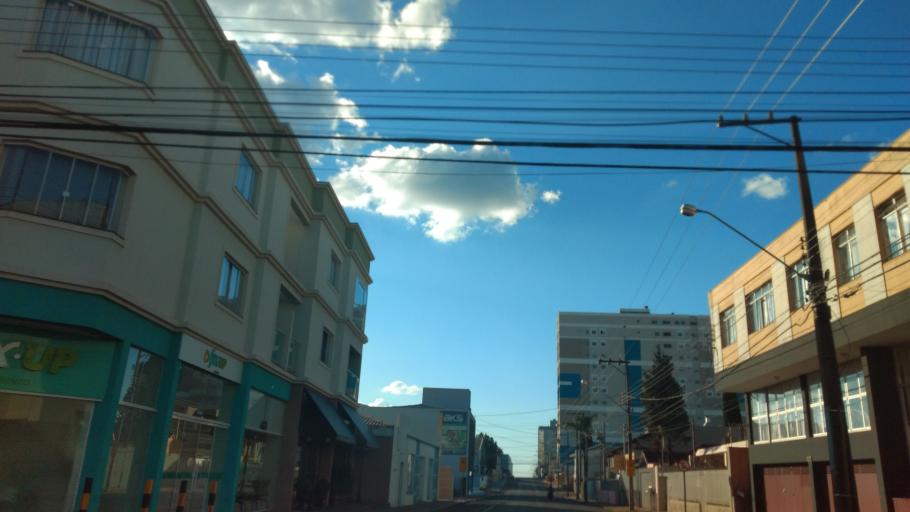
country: BR
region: Parana
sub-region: Guarapuava
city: Guarapuava
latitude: -25.3916
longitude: -51.4753
